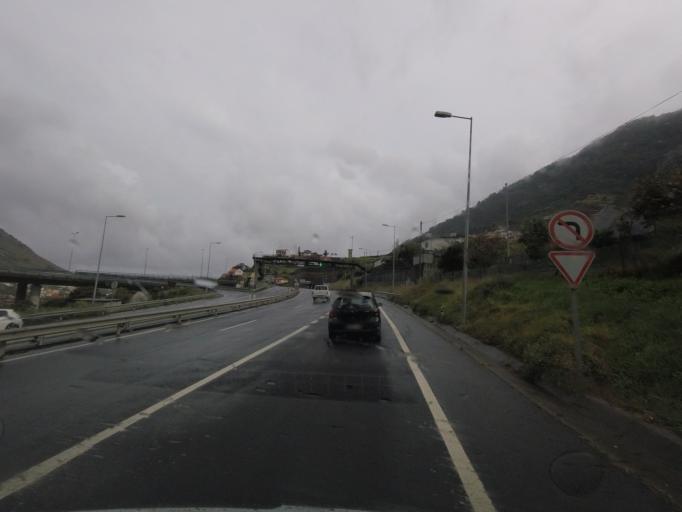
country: PT
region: Madeira
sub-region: Machico
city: Machico
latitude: 32.7283
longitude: -16.7801
